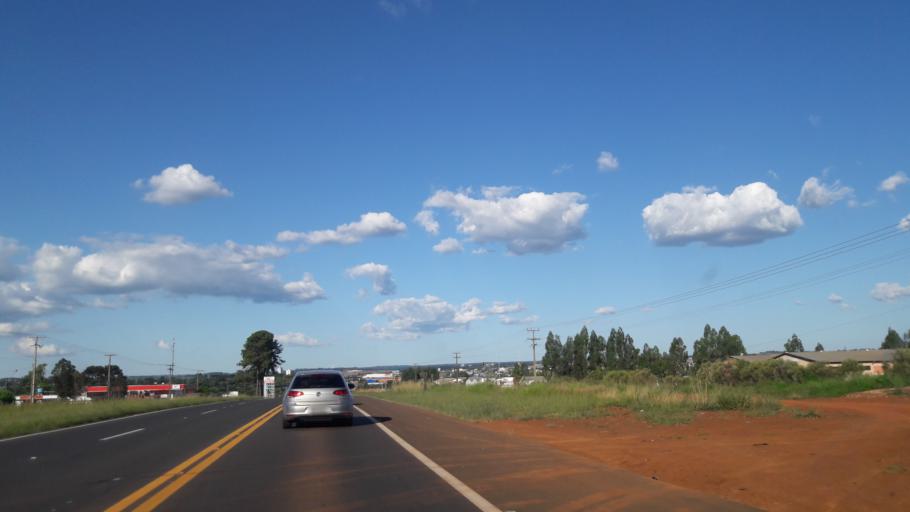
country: BR
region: Parana
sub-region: Guarapuava
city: Guarapuava
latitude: -25.3814
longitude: -51.5099
